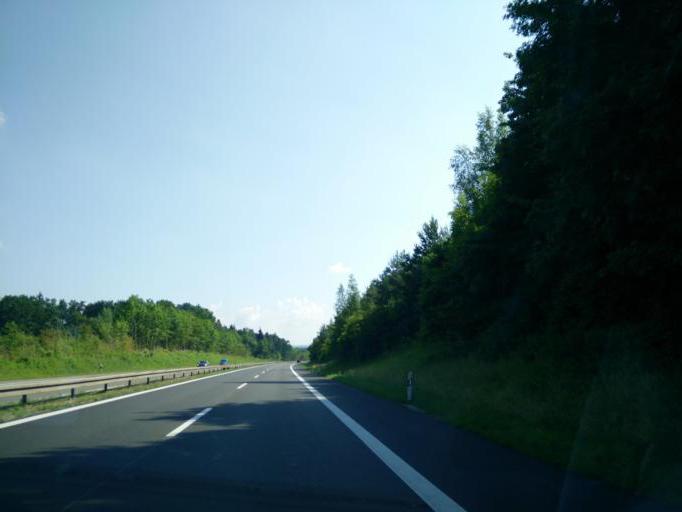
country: DE
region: Baden-Wuerttemberg
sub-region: Regierungsbezirk Stuttgart
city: Schlaitdorf
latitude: 48.6068
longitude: 9.2008
